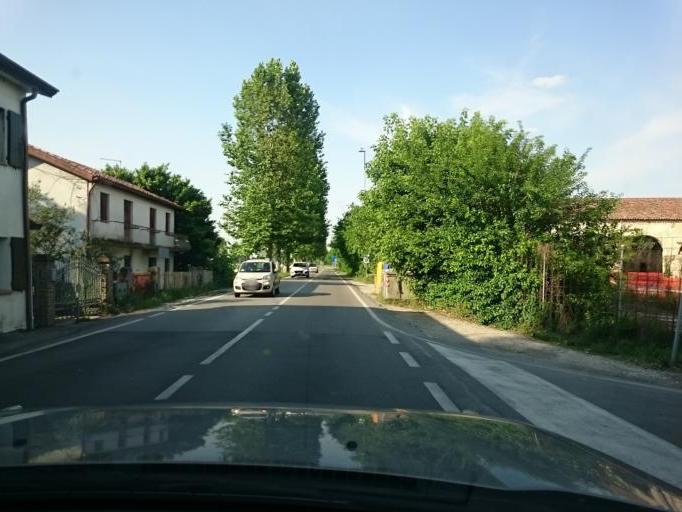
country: IT
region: Veneto
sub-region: Provincia di Padova
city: Abano Terme
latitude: 45.3562
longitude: 11.8094
